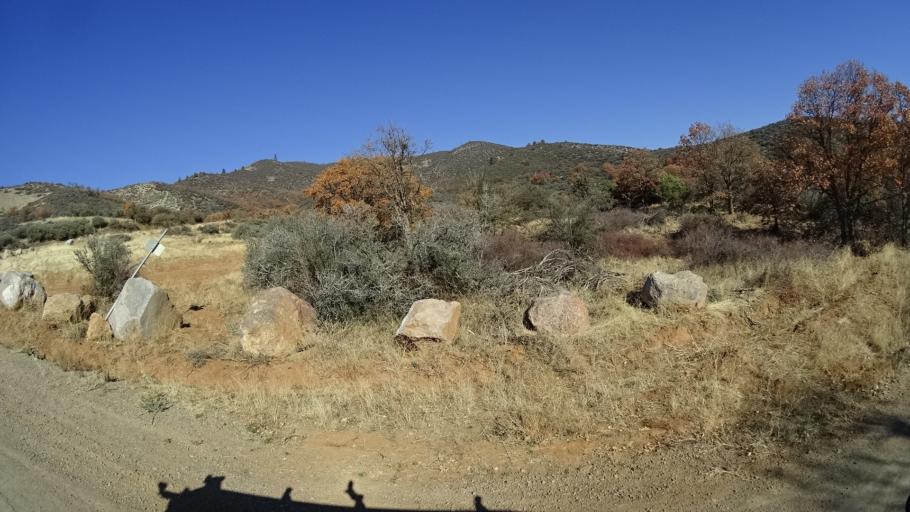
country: US
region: California
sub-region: Siskiyou County
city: Yreka
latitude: 41.7430
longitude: -122.6564
